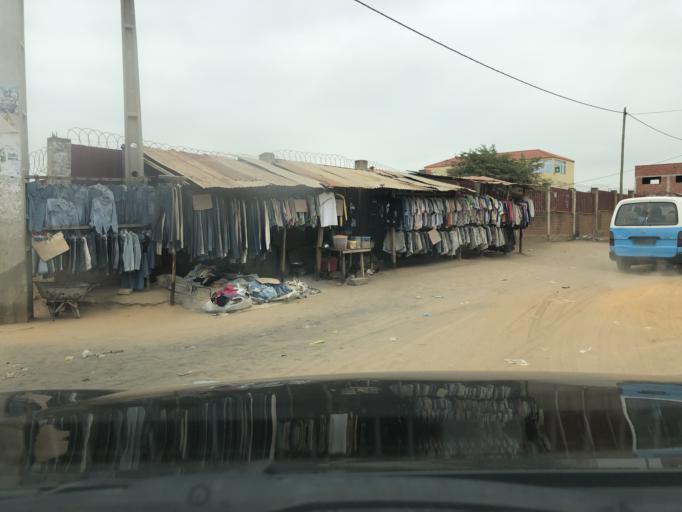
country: AO
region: Luanda
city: Luanda
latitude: -8.9372
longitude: 13.2259
